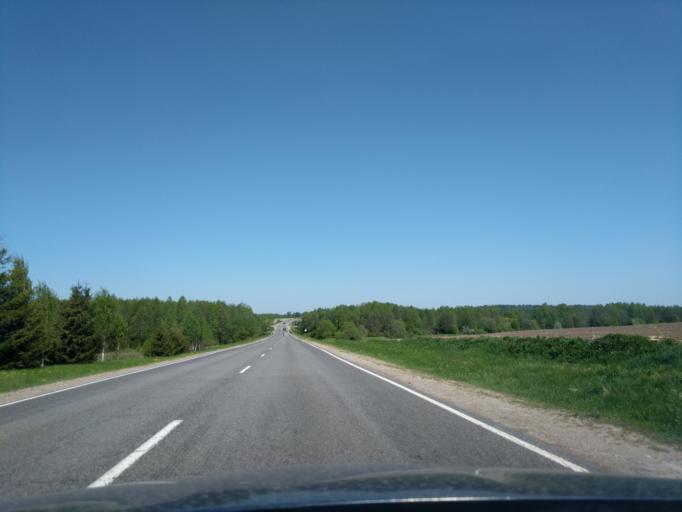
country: BY
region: Minsk
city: Il'ya
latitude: 54.2955
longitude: 27.4816
